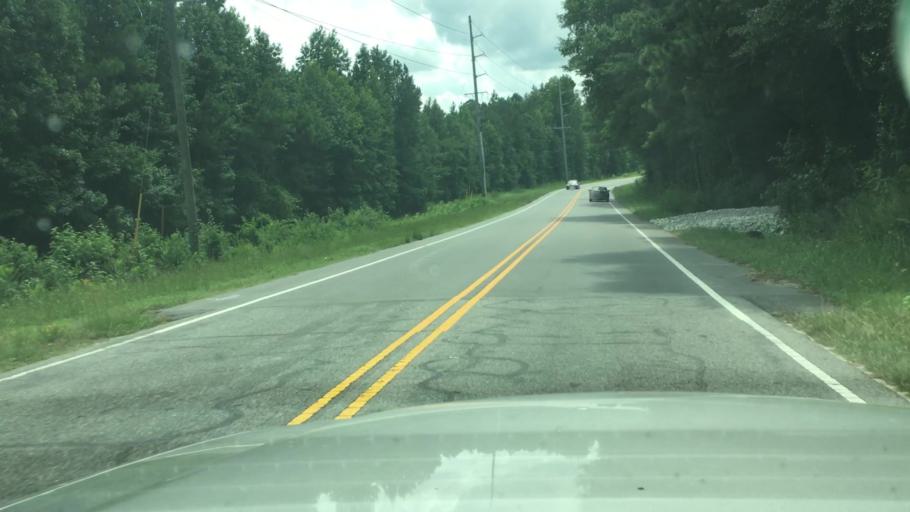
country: US
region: North Carolina
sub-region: Hoke County
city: Rockfish
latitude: 35.0119
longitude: -79.0133
